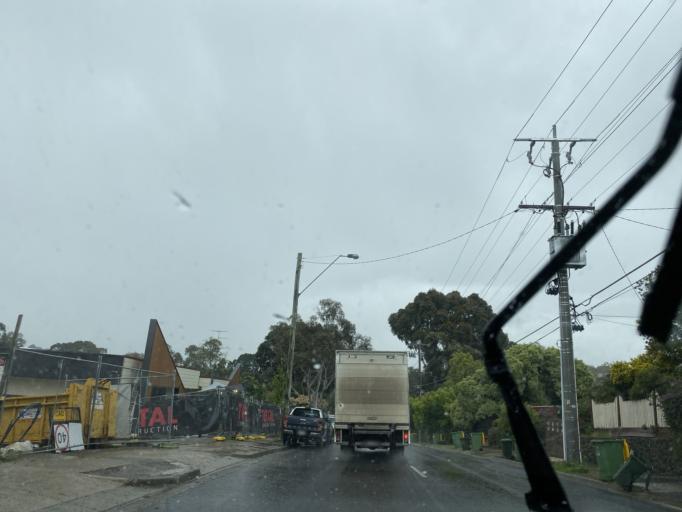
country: AU
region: Victoria
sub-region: Banyule
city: Montmorency
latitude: -37.7217
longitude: 145.1133
